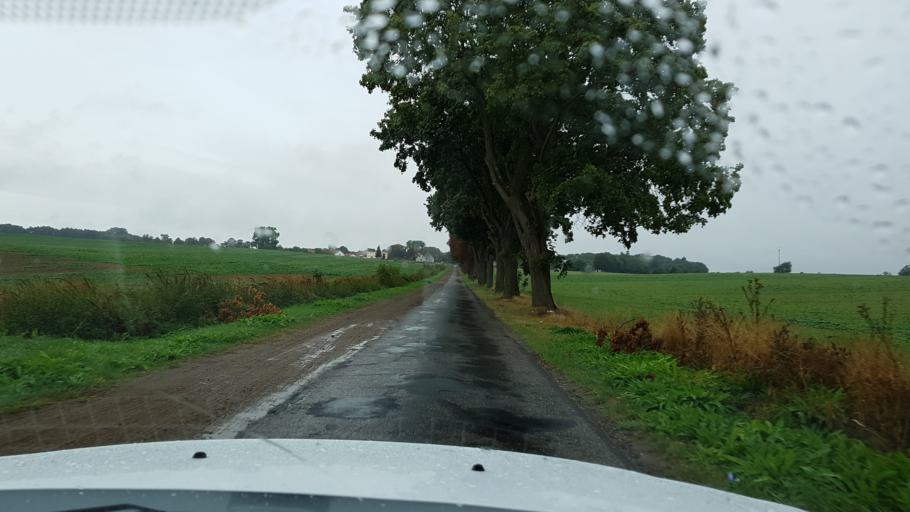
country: DE
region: Brandenburg
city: Schwedt (Oder)
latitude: 53.0240
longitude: 14.3219
